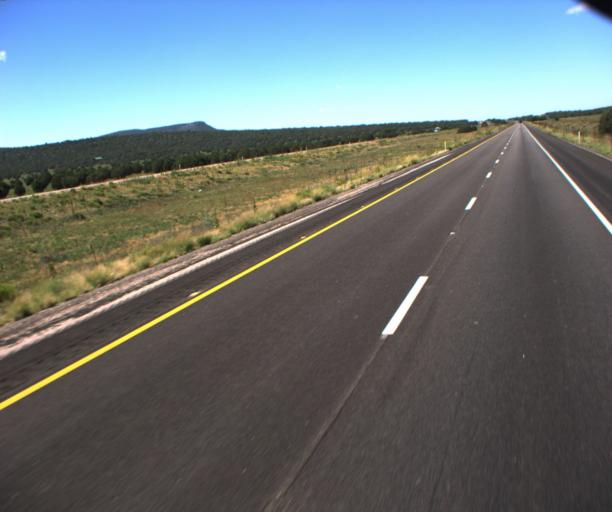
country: US
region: Arizona
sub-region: Mohave County
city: Peach Springs
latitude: 35.2308
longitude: -113.2227
